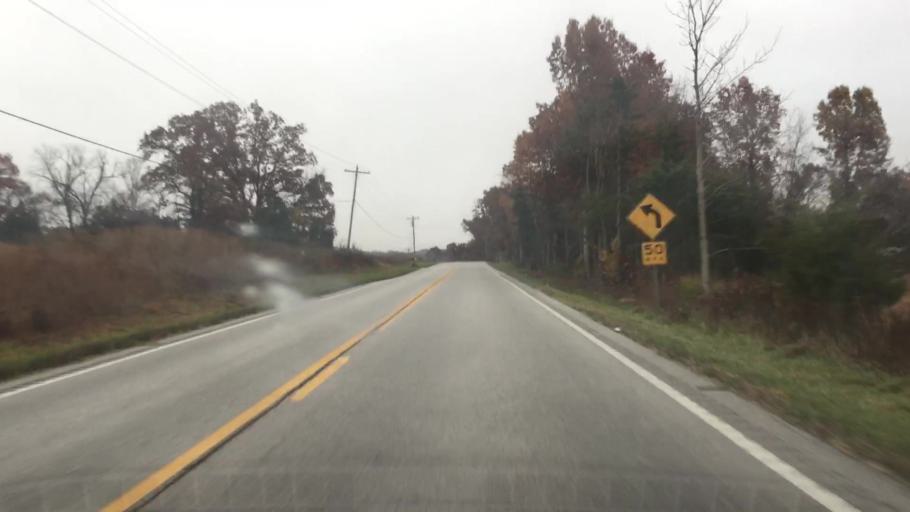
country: US
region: Missouri
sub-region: Callaway County
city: Fulton
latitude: 38.8855
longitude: -92.0953
